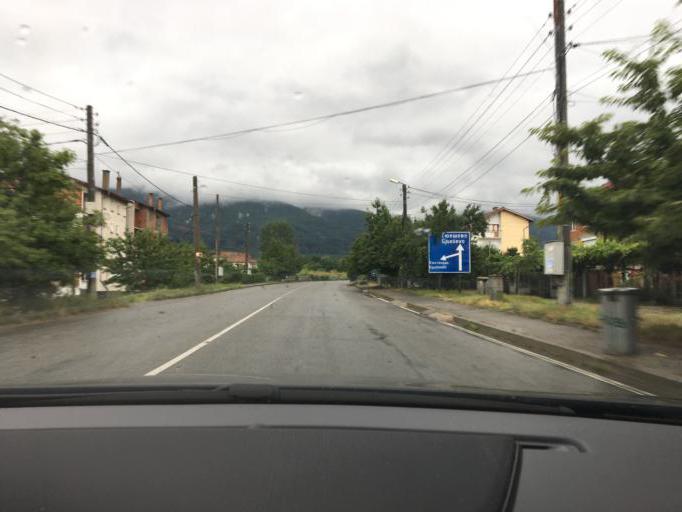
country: BG
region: Kyustendil
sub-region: Obshtina Kyustendil
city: Kyustendil
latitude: 42.2749
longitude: 22.6549
